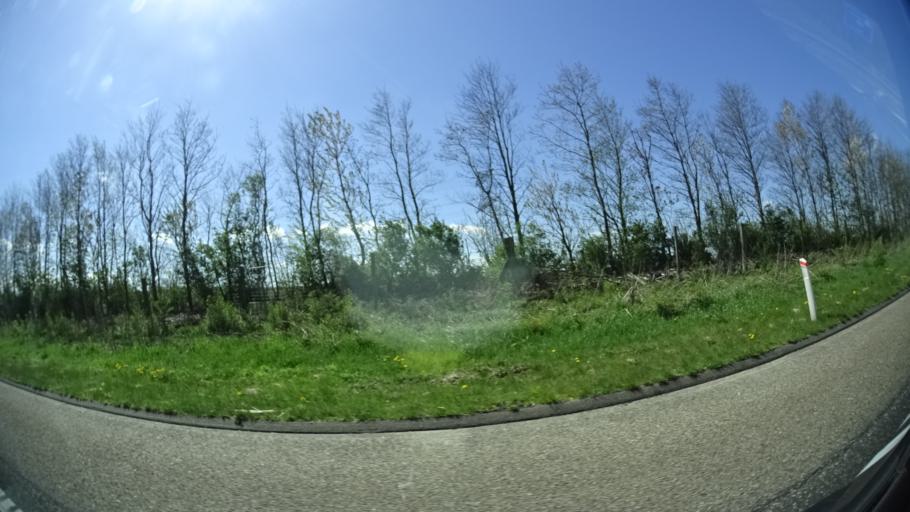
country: DK
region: Central Jutland
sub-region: Arhus Kommune
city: Trige
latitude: 56.3033
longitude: 10.1231
